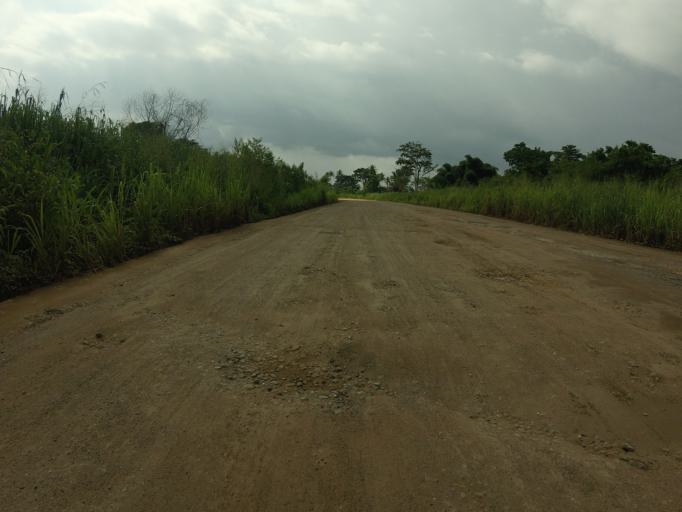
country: GH
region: Volta
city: Kpandu
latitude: 6.9830
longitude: 0.4472
